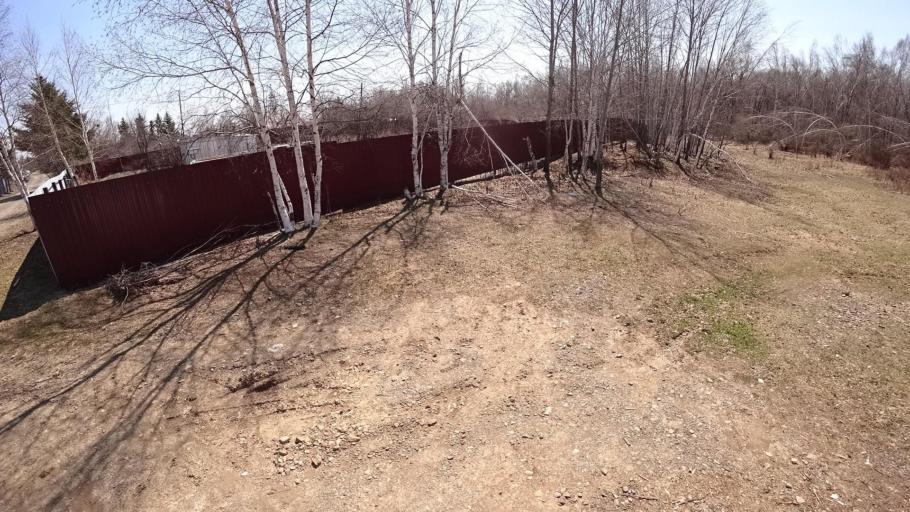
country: RU
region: Khabarovsk Krai
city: Khurba
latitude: 50.4142
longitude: 136.8602
